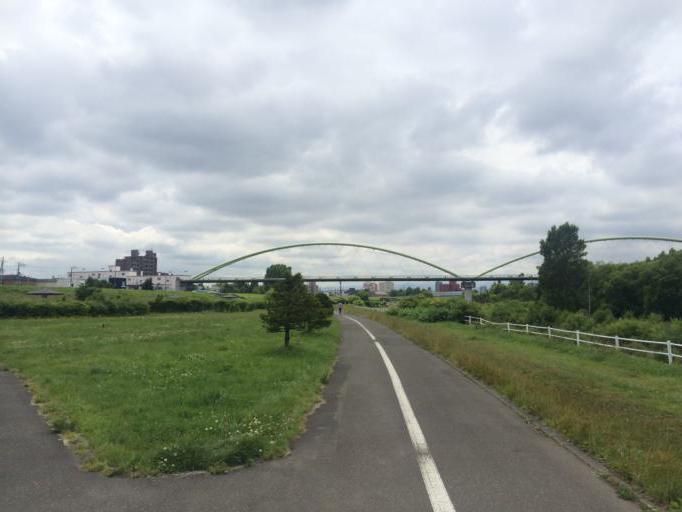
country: JP
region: Hokkaido
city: Sapporo
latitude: 43.0742
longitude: 141.4040
